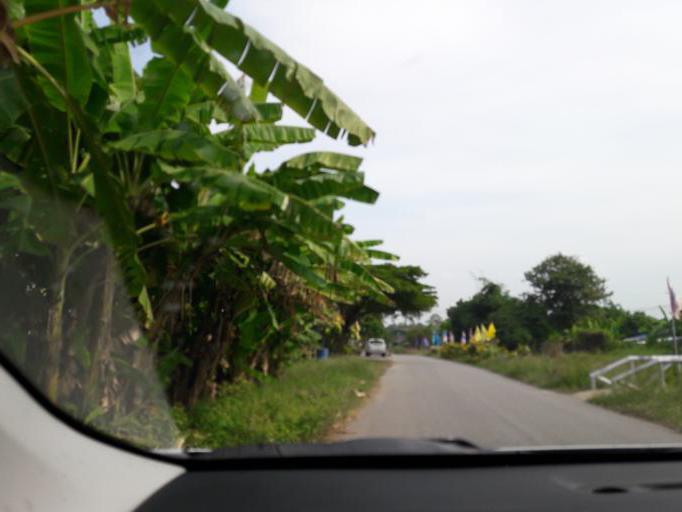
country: TH
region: Ang Thong
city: Ang Thong
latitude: 14.5820
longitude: 100.4762
